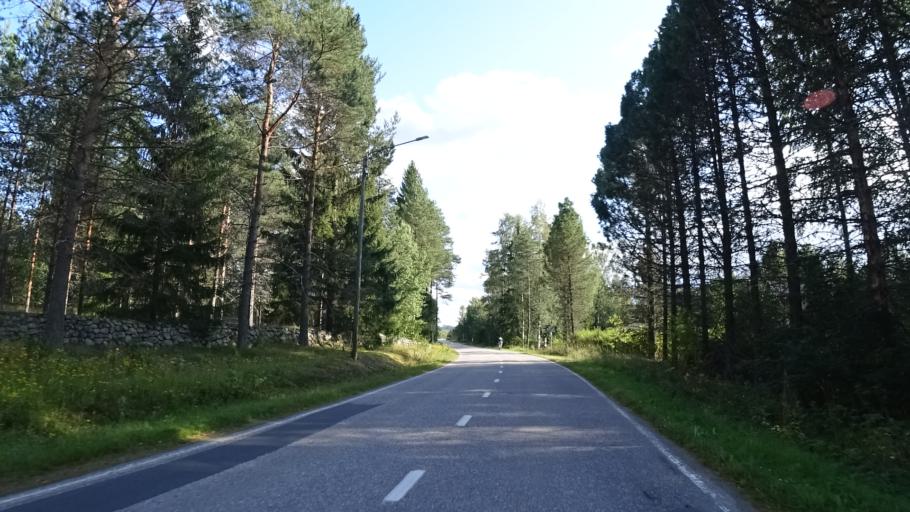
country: FI
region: North Karelia
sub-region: Keski-Karjala
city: Kesaelahti
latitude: 61.8866
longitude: 29.8383
